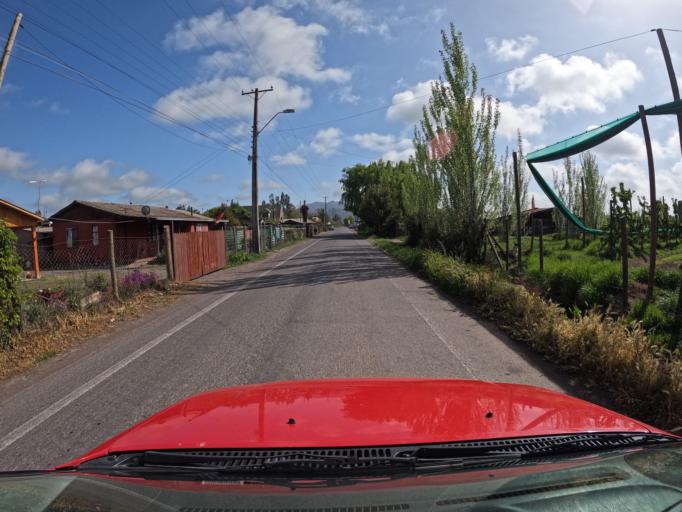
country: CL
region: Maule
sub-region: Provincia de Curico
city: Teno
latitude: -34.8803
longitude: -71.2258
